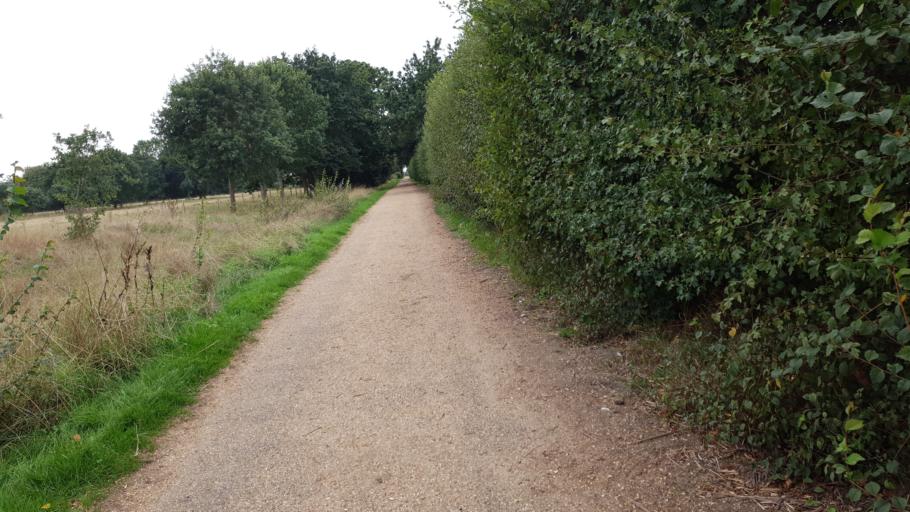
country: GB
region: England
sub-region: Essex
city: Manningtree
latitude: 51.9435
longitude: 1.0341
